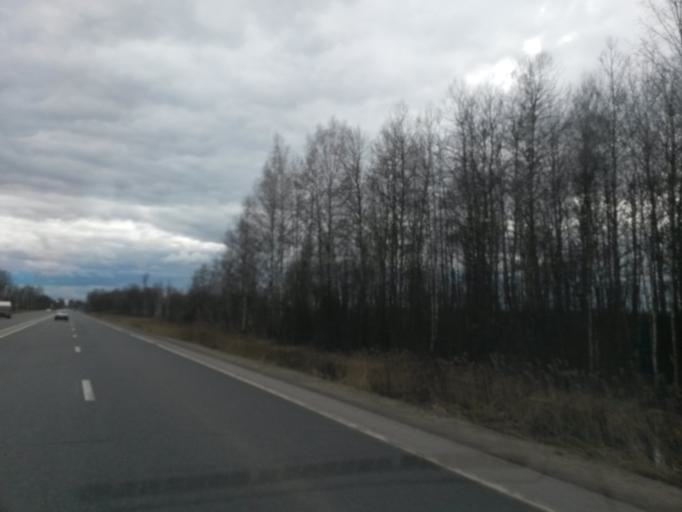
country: RU
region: Jaroslavl
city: Rostov
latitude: 57.2276
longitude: 39.4654
